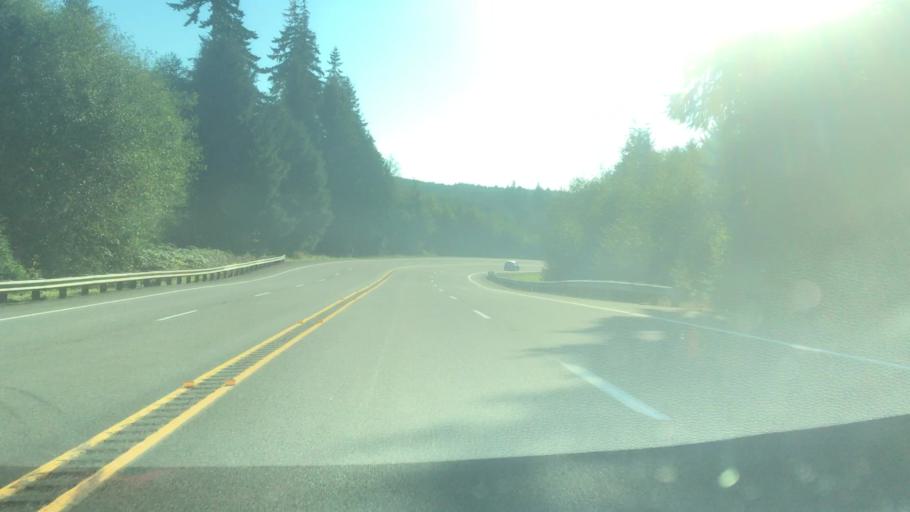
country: US
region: Washington
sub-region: Pacific County
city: South Bend
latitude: 46.6815
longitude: -123.8931
